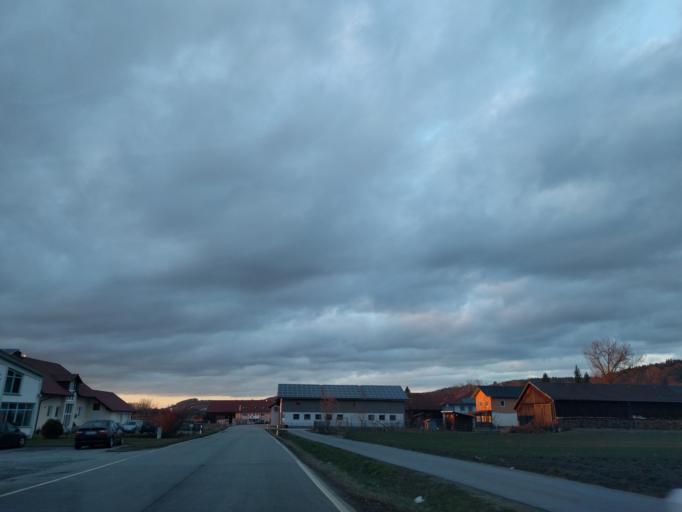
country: DE
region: Bavaria
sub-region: Lower Bavaria
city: Hofkirchen
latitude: 48.6993
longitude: 13.1140
